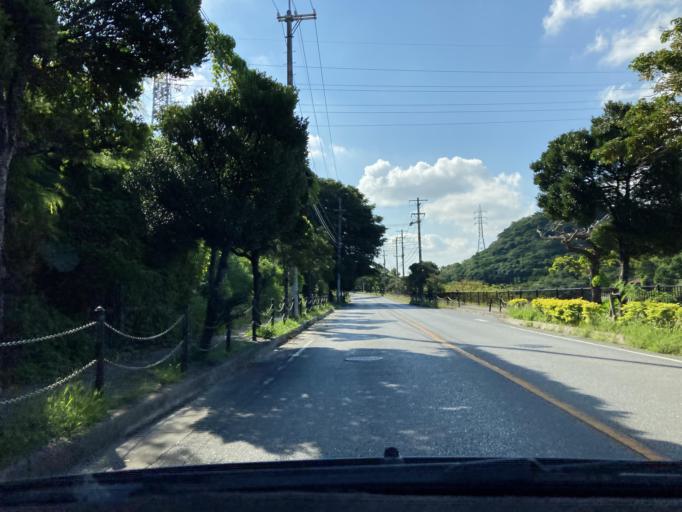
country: JP
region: Okinawa
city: Naha-shi
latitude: 26.2116
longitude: 127.7193
